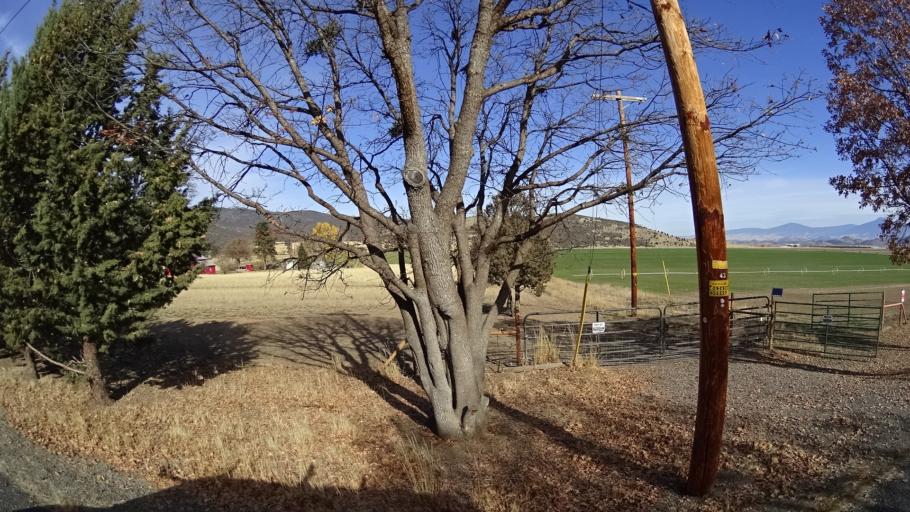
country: US
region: California
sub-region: Siskiyou County
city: Montague
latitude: 41.5390
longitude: -122.5739
